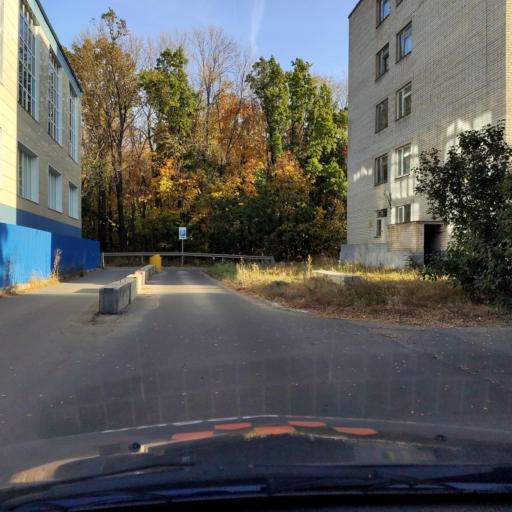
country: RU
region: Voronezj
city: Podgornoye
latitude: 51.8094
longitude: 39.2228
